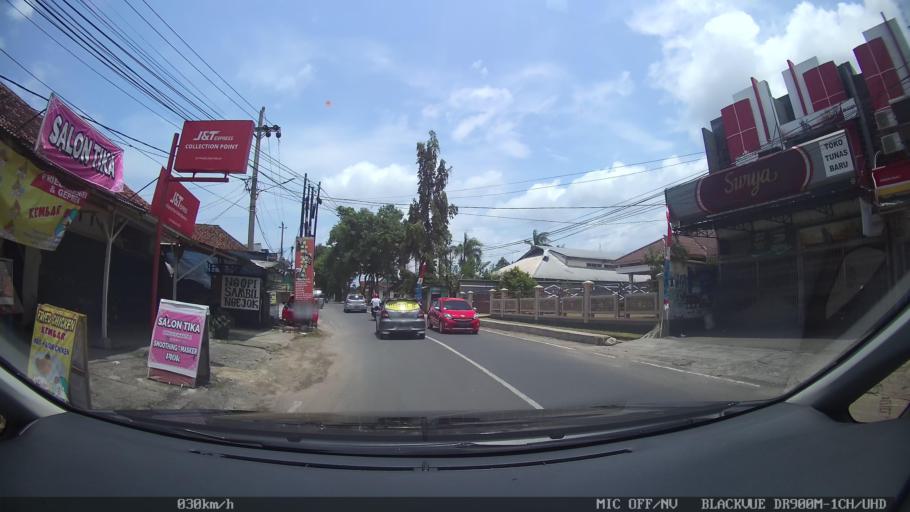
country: ID
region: Lampung
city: Kedaton
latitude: -5.3945
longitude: 105.2488
